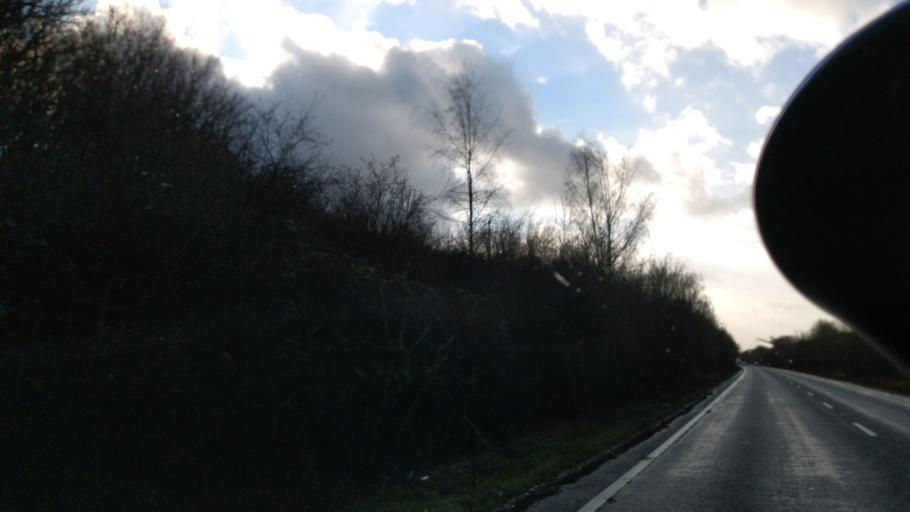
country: GB
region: England
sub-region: Somerset
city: Frome
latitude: 51.2303
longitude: -2.2981
